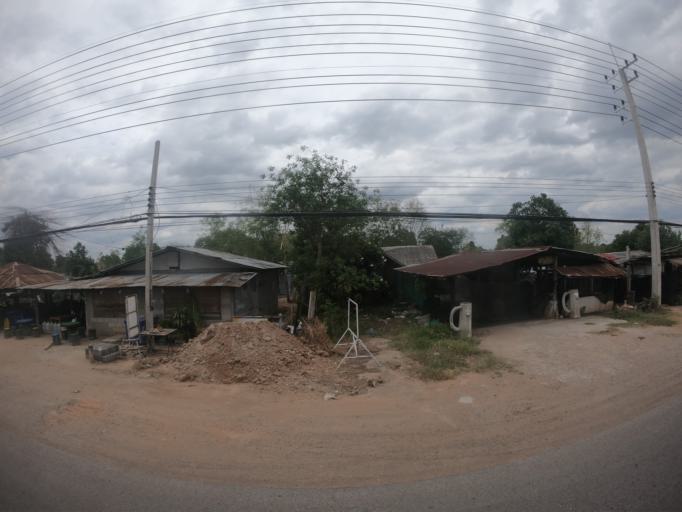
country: TH
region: Nakhon Ratchasima
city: Chok Chai
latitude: 14.8246
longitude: 102.1808
